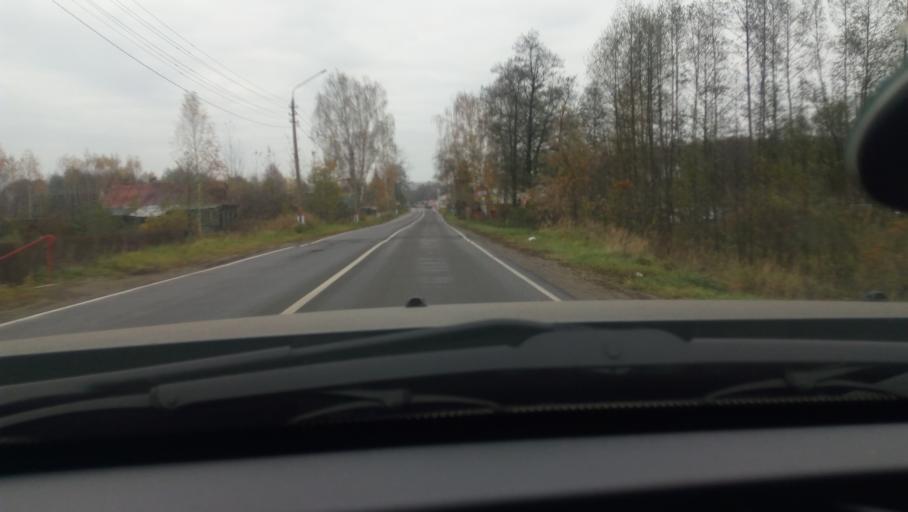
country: RU
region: Moskovskaya
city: Likino-Dulevo
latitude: 55.7013
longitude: 38.9414
